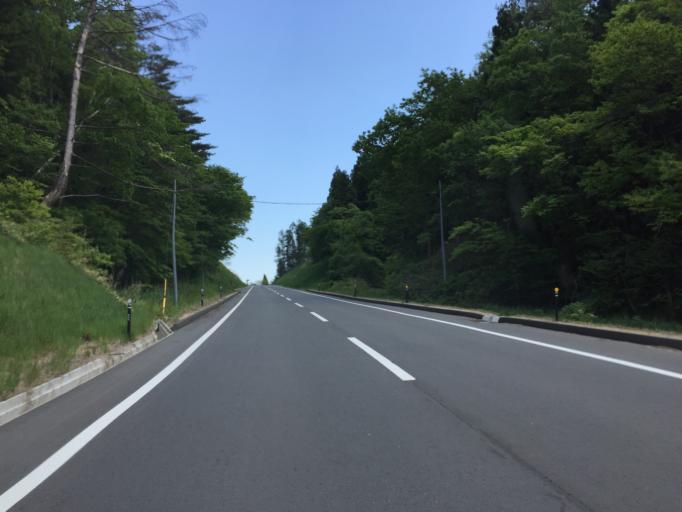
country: JP
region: Fukushima
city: Funehikimachi-funehiki
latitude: 37.5114
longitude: 140.6954
